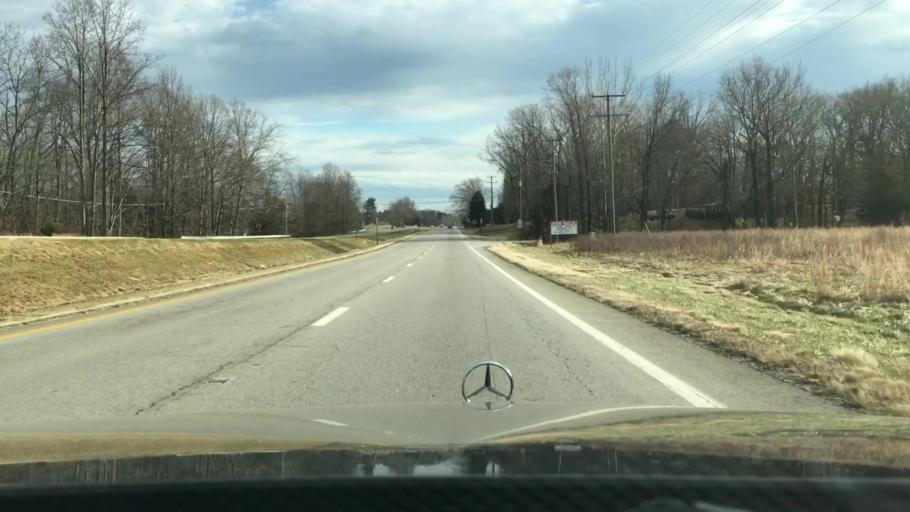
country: US
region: Virginia
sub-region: Pittsylvania County
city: Mount Hermon
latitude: 36.7163
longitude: -79.3795
